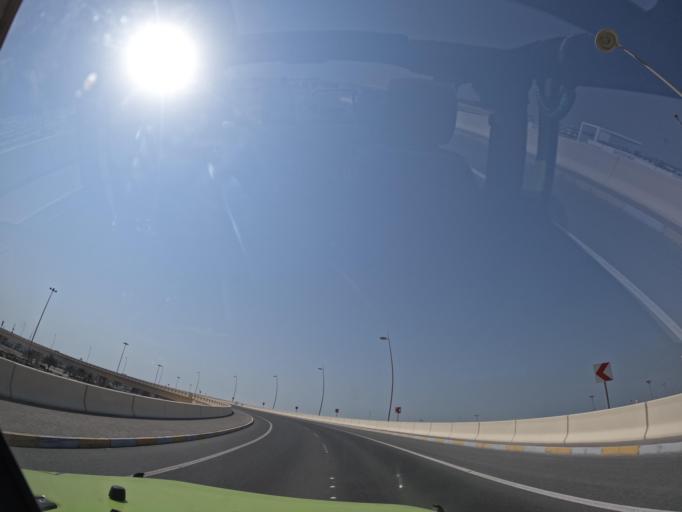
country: AE
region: Abu Dhabi
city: Abu Dhabi
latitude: 24.4953
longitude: 54.6149
